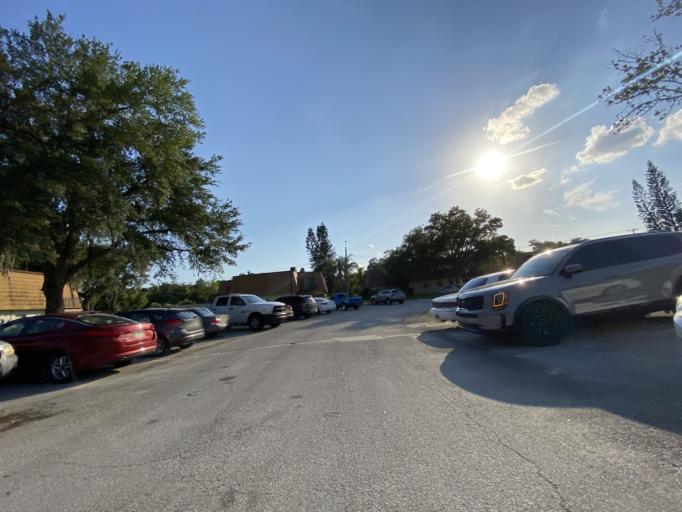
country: US
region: Florida
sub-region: Volusia County
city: Port Orange
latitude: 29.1413
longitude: -81.0115
